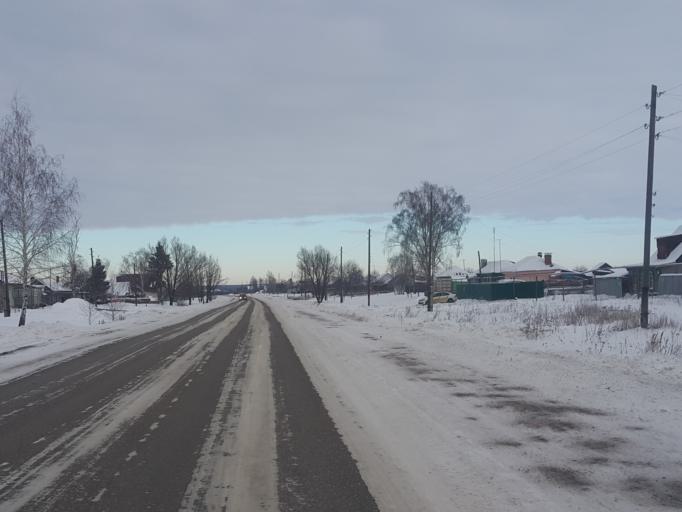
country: RU
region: Tambov
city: Platonovka
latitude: 52.8317
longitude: 41.8086
